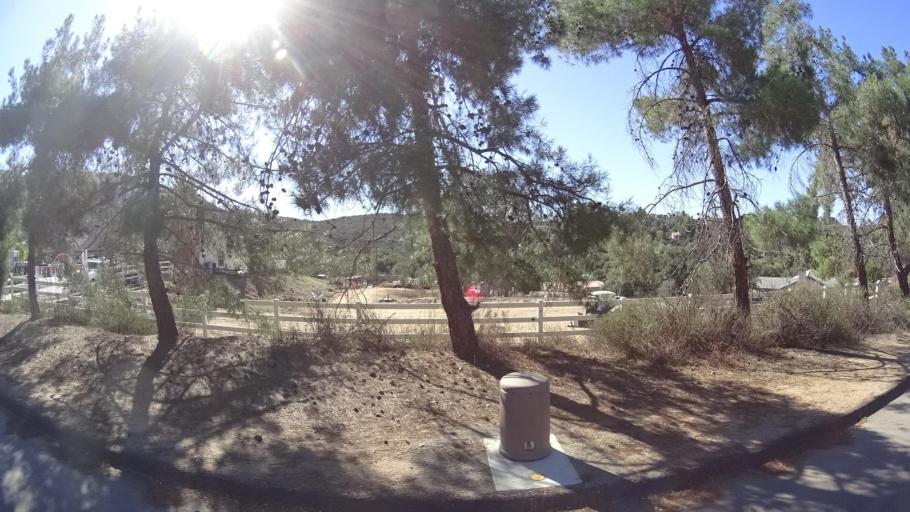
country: US
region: California
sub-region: San Diego County
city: Jamul
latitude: 32.7200
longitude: -116.8489
